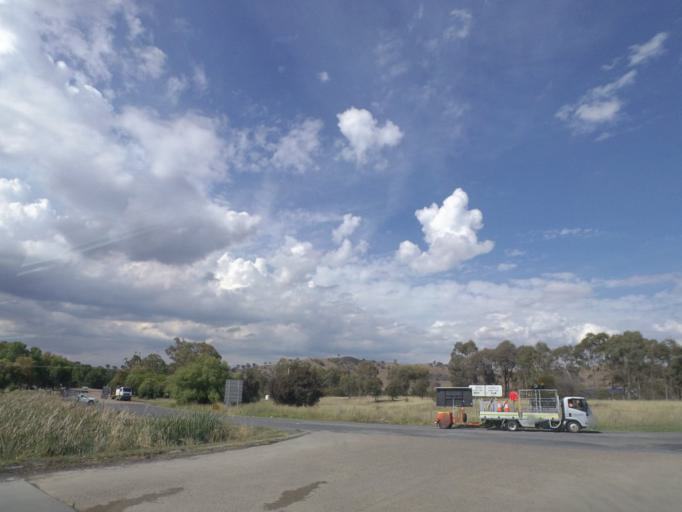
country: AU
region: New South Wales
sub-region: Gundagai
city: Gundagai
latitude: -35.0034
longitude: 148.1107
